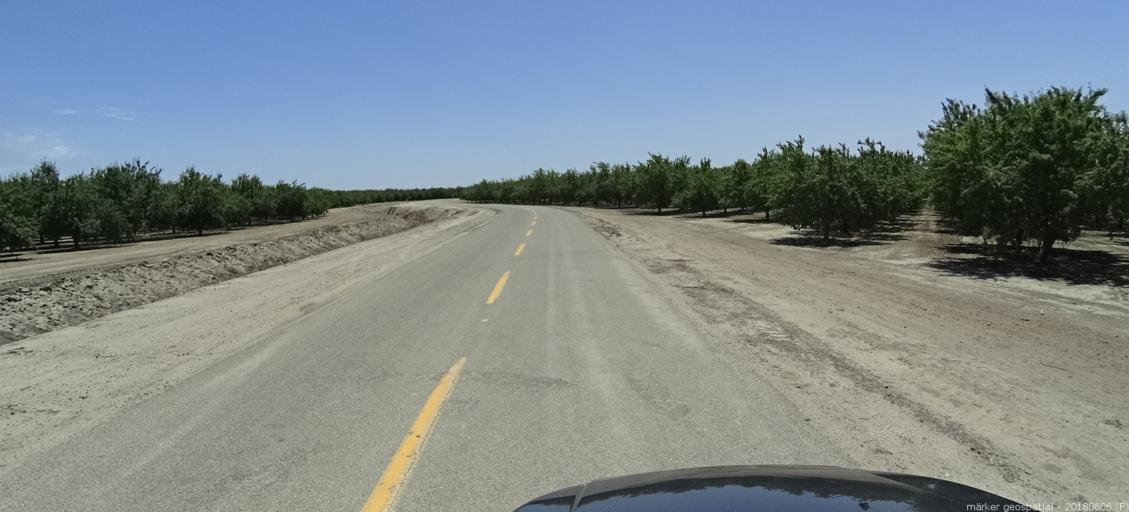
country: US
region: California
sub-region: Fresno County
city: Mendota
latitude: 36.8163
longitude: -120.3667
